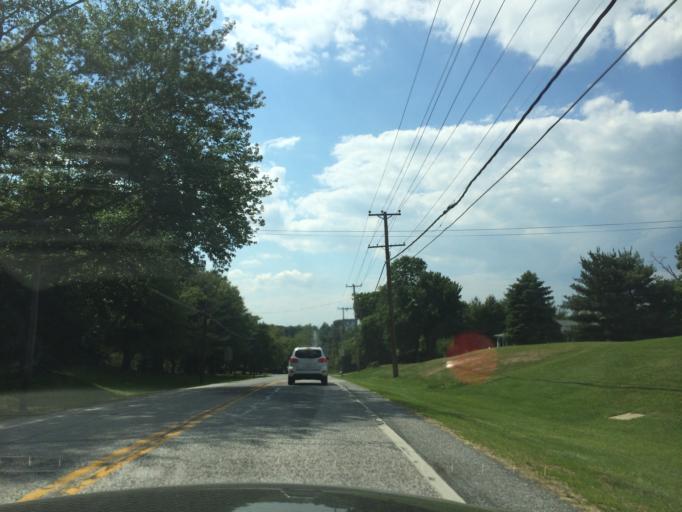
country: US
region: Maryland
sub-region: Carroll County
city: Sykesville
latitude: 39.3014
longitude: -76.9481
